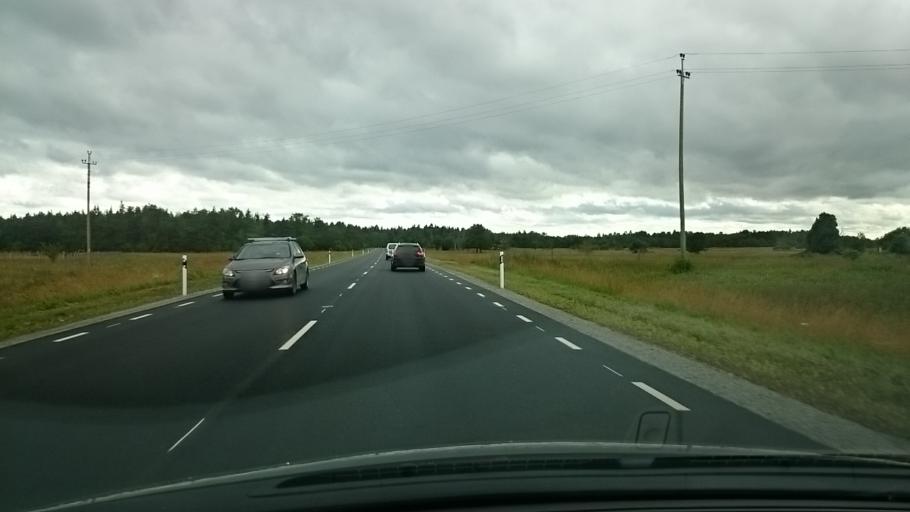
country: EE
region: Harju
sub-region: Keila linn
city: Keila
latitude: 59.2880
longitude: 24.3269
